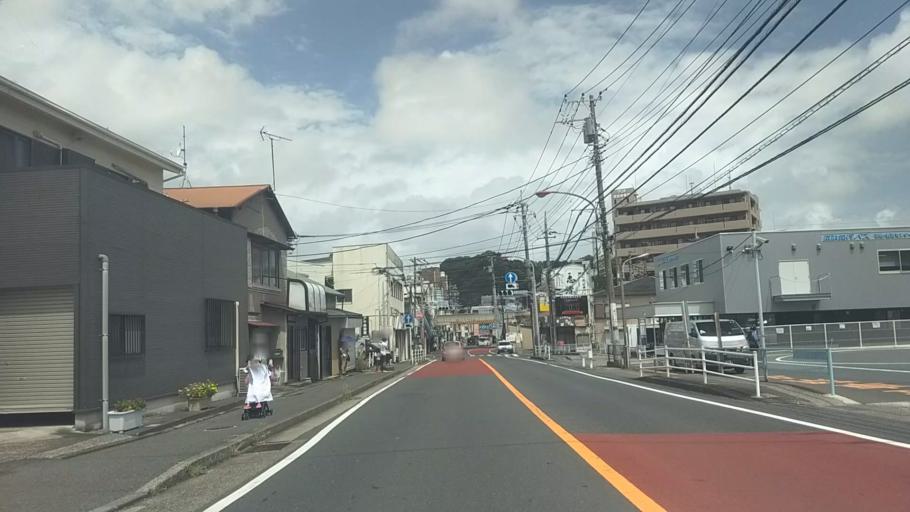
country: JP
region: Kanagawa
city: Yokosuka
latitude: 35.2545
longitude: 139.6654
